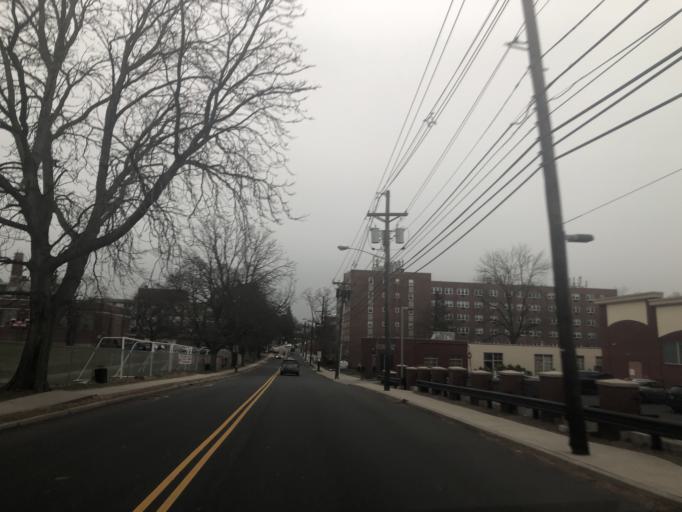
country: US
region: New Jersey
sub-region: Essex County
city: Maplewood
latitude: 40.7377
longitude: -74.2659
